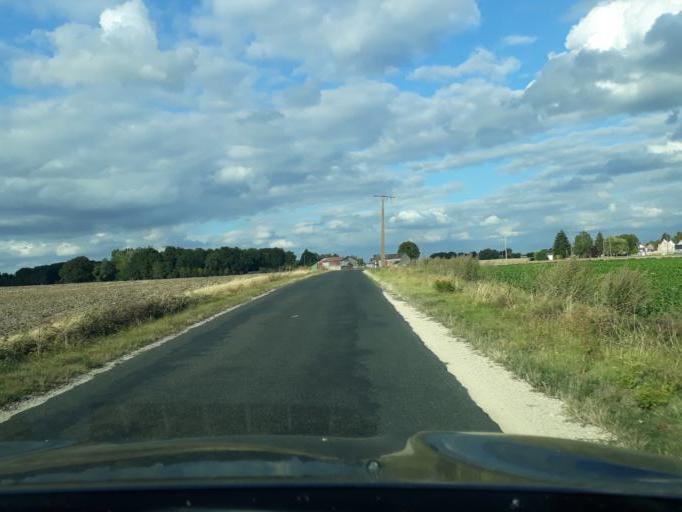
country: FR
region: Centre
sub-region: Departement du Loiret
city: Loury
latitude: 47.9992
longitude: 2.0631
